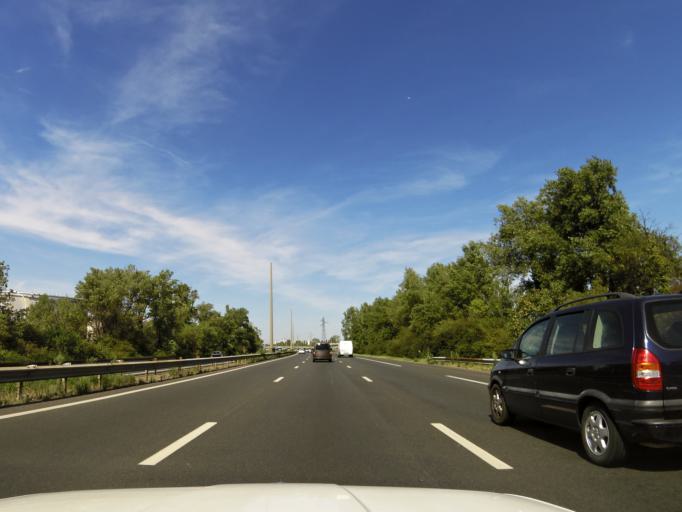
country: FR
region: Rhone-Alpes
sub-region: Departement du Rhone
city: Solaize
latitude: 45.6541
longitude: 4.8386
